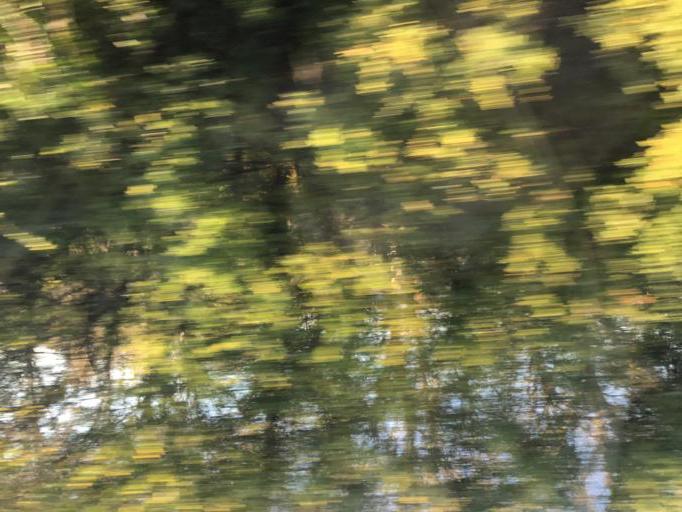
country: DK
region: Capital Region
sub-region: Hvidovre Kommune
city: Hvidovre
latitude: 55.6412
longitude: 12.5017
